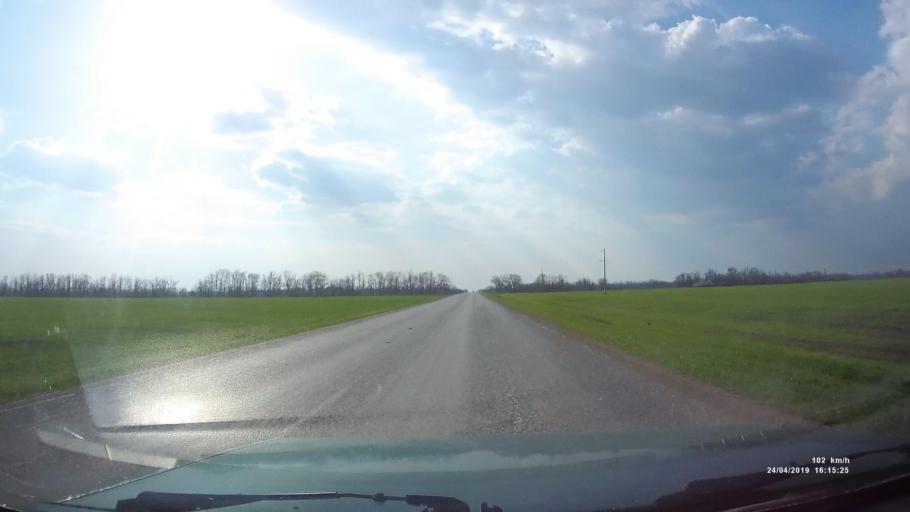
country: RU
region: Rostov
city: Sovetskoye
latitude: 46.7573
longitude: 42.1818
